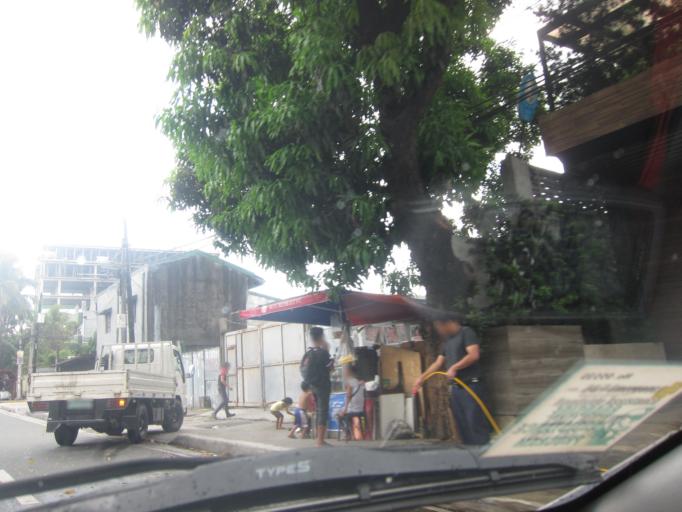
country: PH
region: Metro Manila
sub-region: Quezon City
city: Quezon City
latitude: 14.6399
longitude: 121.0548
